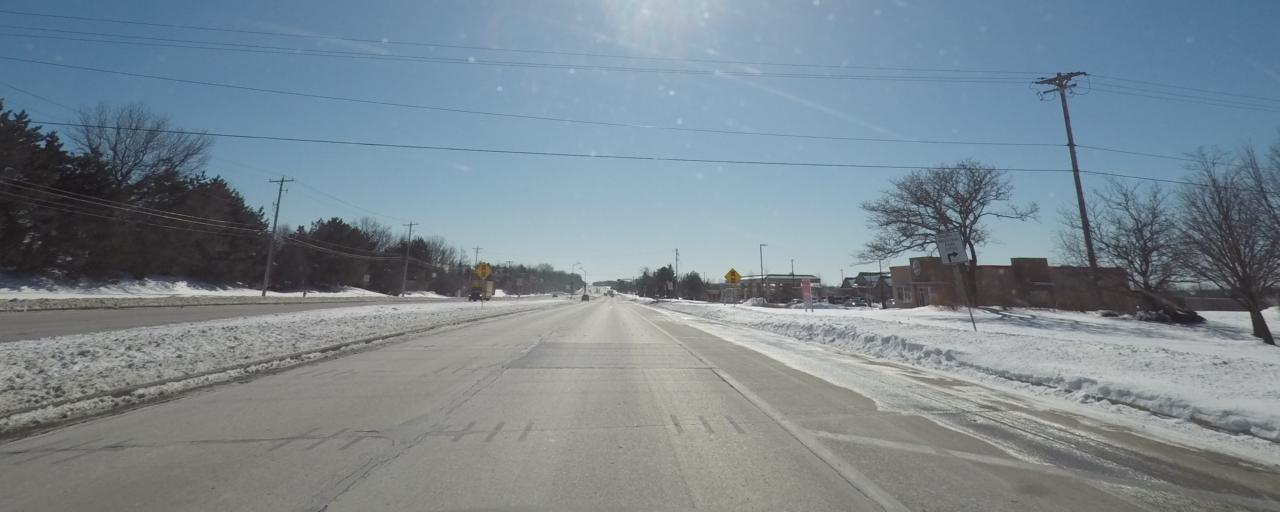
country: US
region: Wisconsin
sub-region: Waukesha County
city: New Berlin
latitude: 43.0081
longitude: -88.1080
